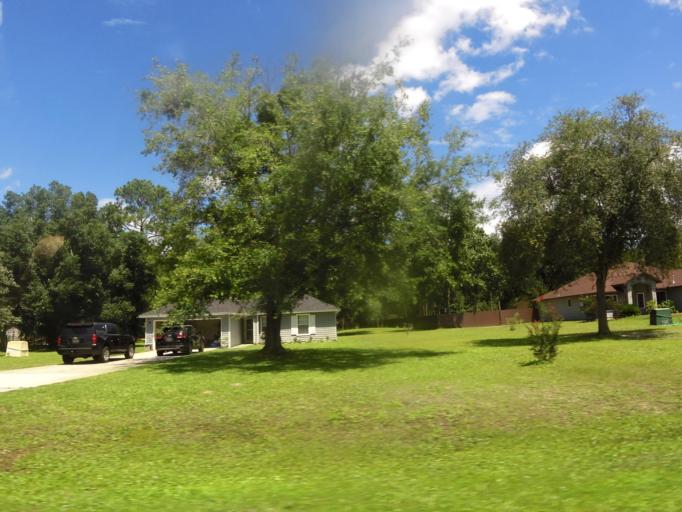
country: US
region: Florida
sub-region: Nassau County
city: Yulee
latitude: 30.6532
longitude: -81.5432
